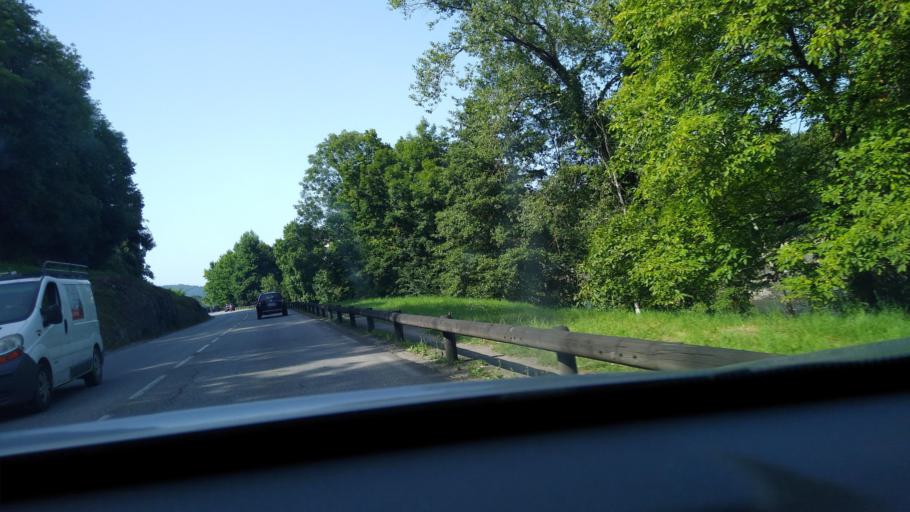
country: FR
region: Midi-Pyrenees
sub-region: Departement de l'Ariege
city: Saint-Lizier
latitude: 42.9955
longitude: 1.1364
